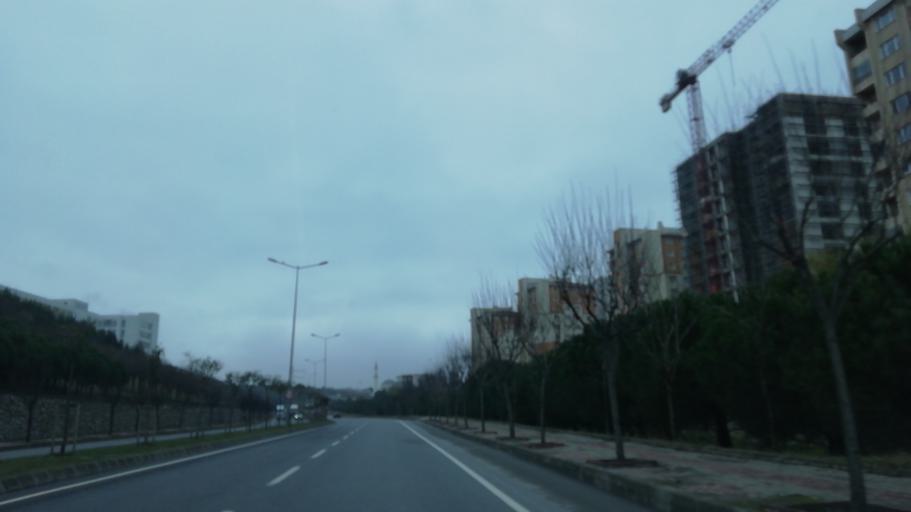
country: TR
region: Istanbul
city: Basaksehir
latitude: 41.1005
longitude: 28.8011
